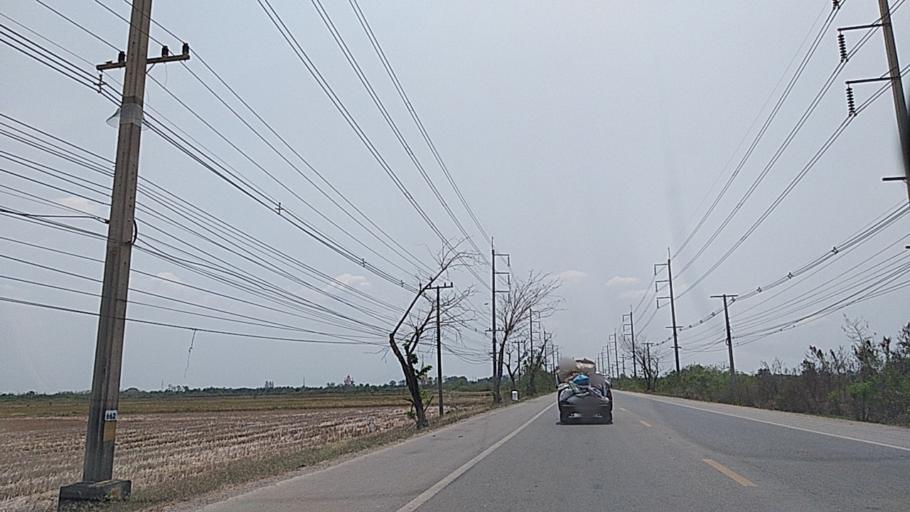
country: TH
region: Chachoengsao
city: Bang Nam Priao
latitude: 13.8132
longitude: 101.0535
